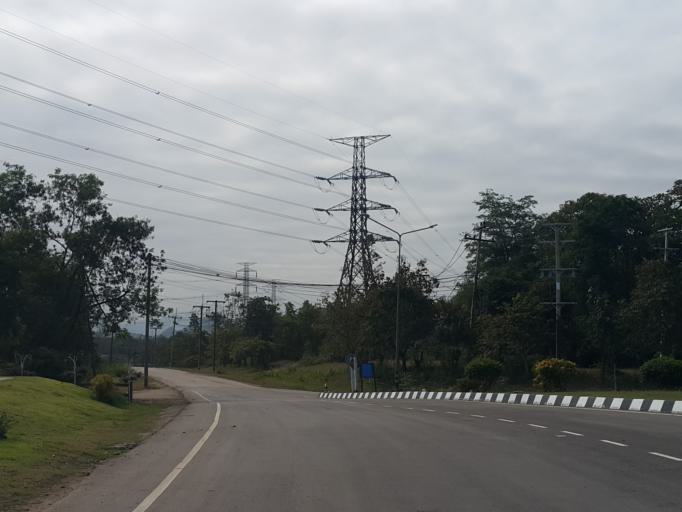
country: TH
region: Lampang
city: Mae Mo
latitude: 18.2966
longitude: 99.7400
